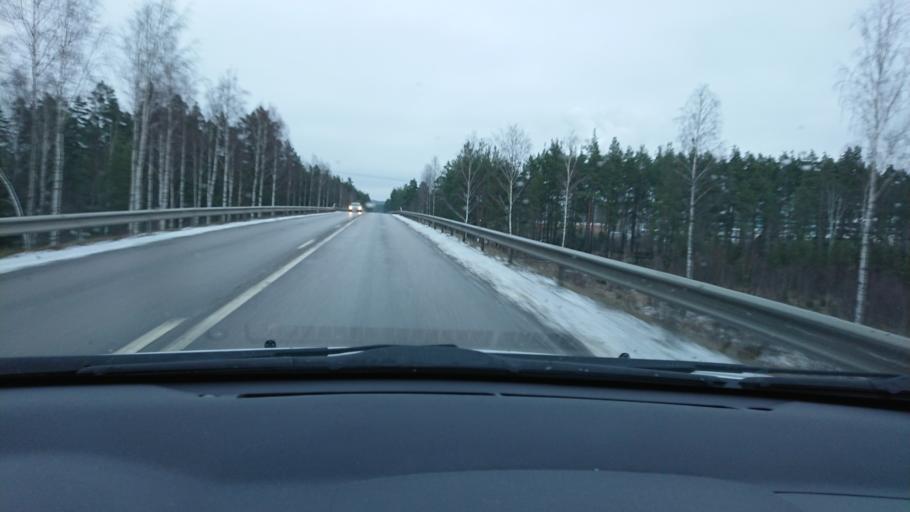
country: SE
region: Kalmar
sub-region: Hultsfreds Kommun
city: Hultsfred
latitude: 57.5038
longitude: 15.8259
